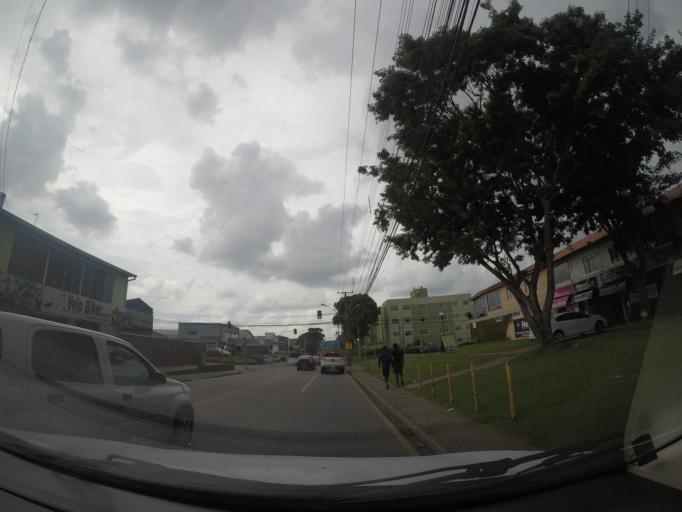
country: BR
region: Parana
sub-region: Sao Jose Dos Pinhais
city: Sao Jose dos Pinhais
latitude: -25.5231
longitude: -49.2425
